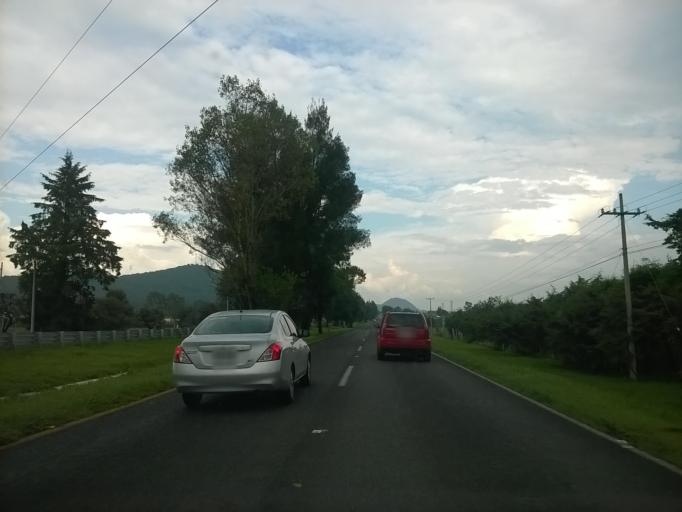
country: MX
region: Michoacan
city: Cuanajo
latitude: 19.5332
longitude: -101.4977
